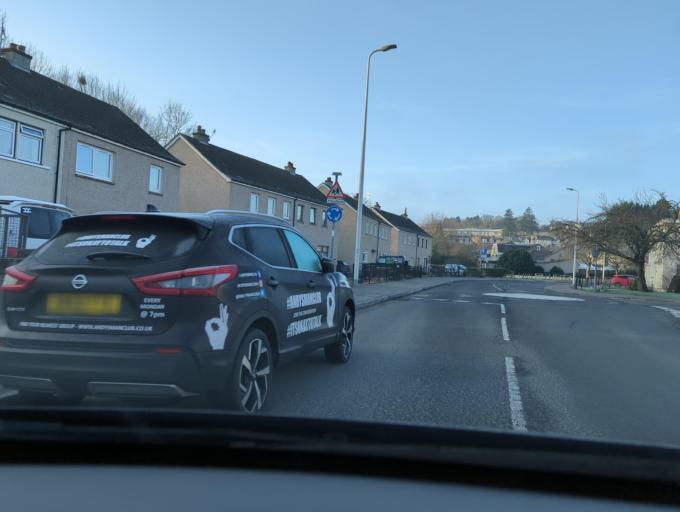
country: GB
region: Scotland
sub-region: Perth and Kinross
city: Perth
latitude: 56.4012
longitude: -3.4547
